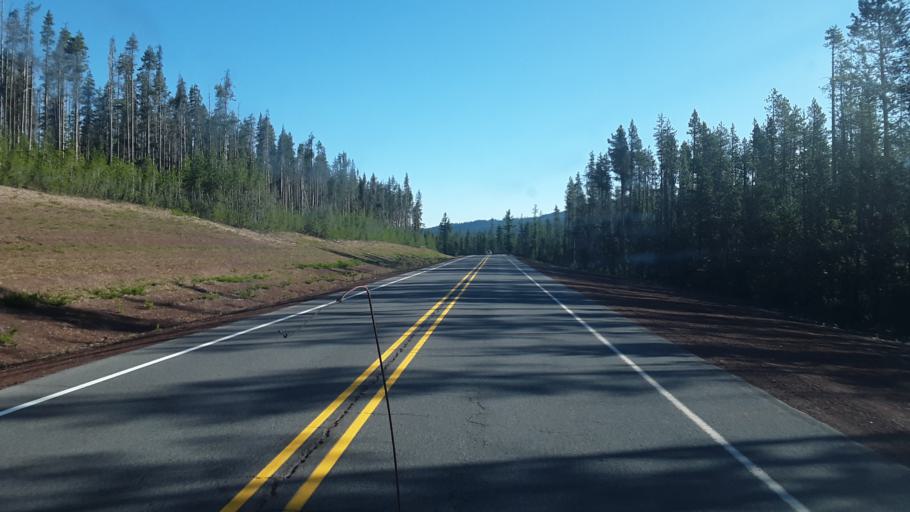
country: US
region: Oregon
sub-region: Lane County
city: Oakridge
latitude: 43.1031
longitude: -122.1302
